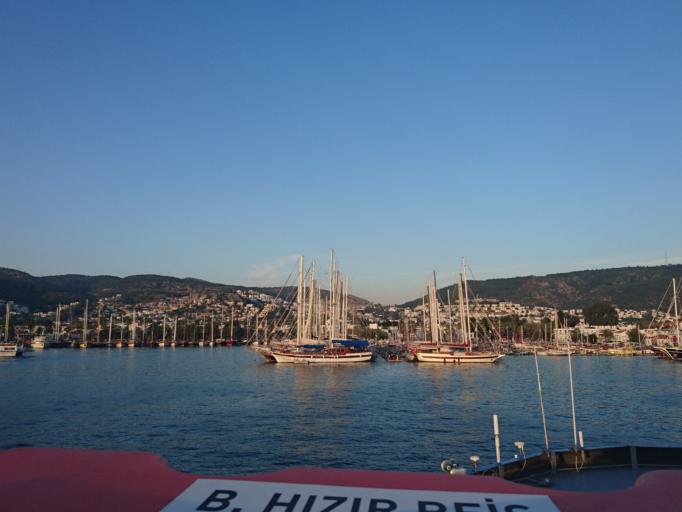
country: TR
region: Mugla
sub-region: Bodrum
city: Bodrum
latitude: 37.0324
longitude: 27.4262
